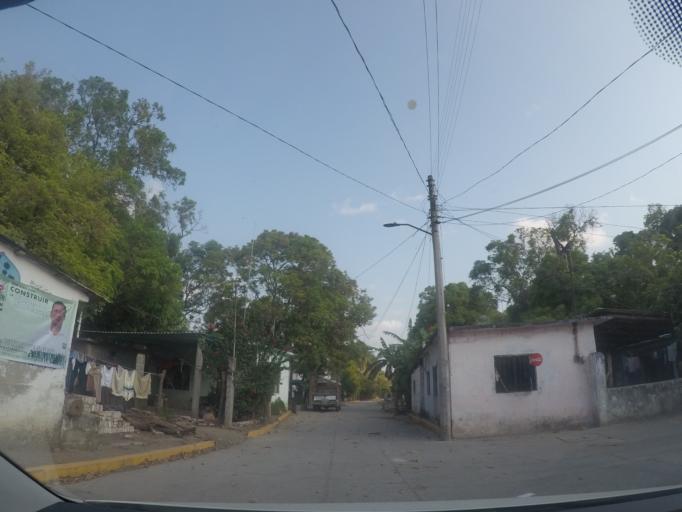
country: MX
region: Oaxaca
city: San Jeronimo Ixtepec
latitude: 16.5898
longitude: -95.1623
